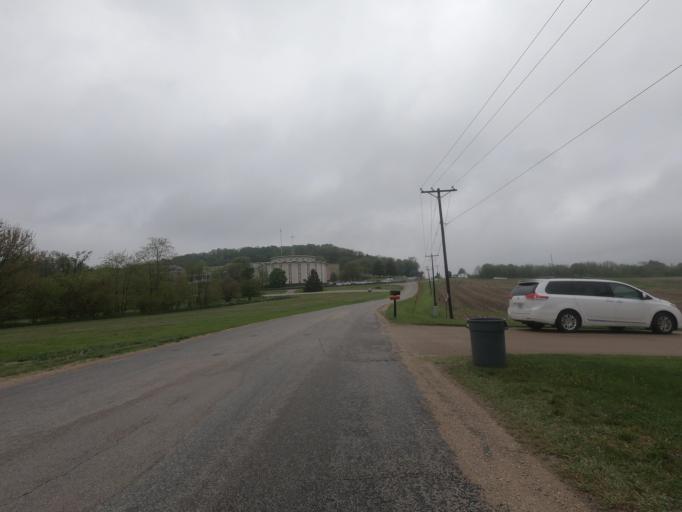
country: US
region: Wisconsin
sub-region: Grant County
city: Hazel Green
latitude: 42.5220
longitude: -90.5389
